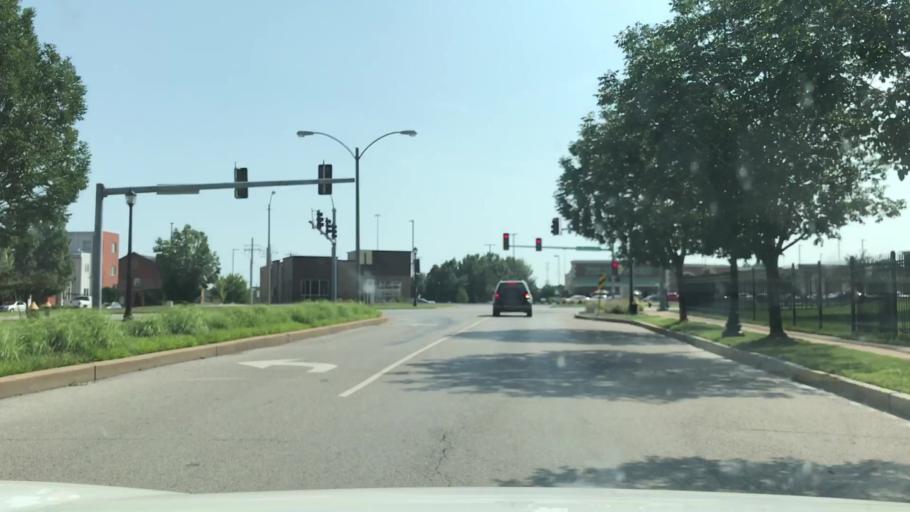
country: US
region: Missouri
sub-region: City of Saint Louis
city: St. Louis
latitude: 38.6137
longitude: -90.2074
